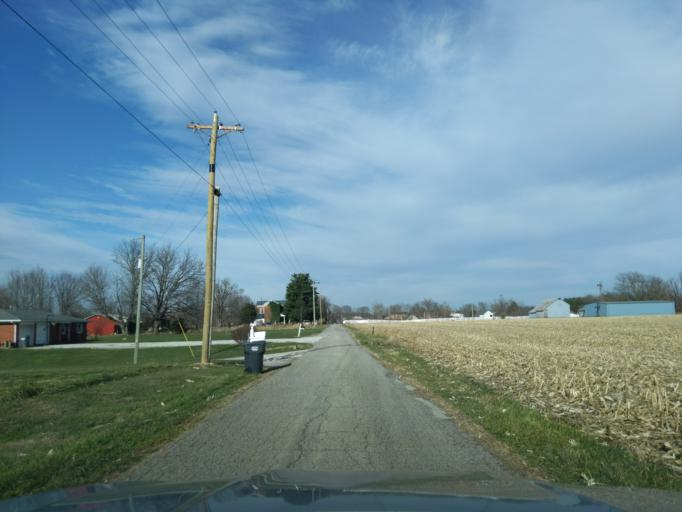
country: US
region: Indiana
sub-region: Decatur County
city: Greensburg
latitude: 39.2061
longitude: -85.4328
